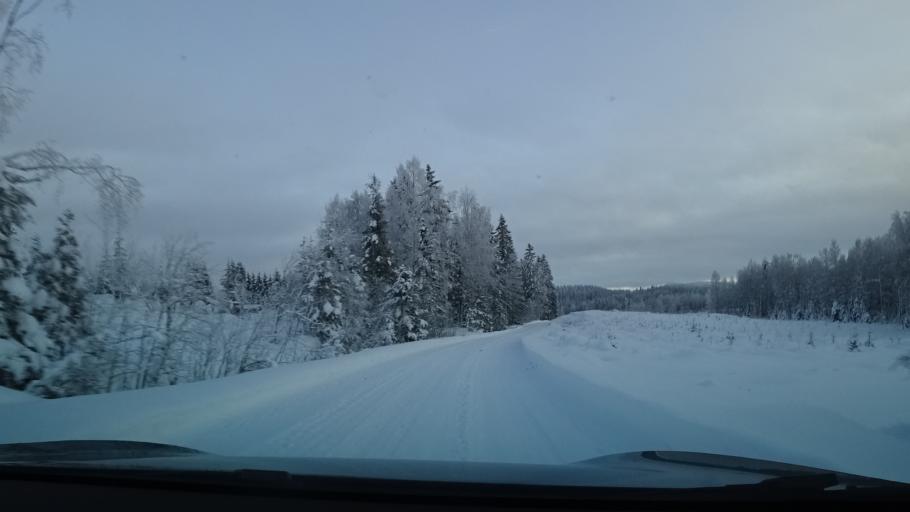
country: FI
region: North Karelia
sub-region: Pielisen Karjala
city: Lieksa
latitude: 63.1046
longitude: 29.7551
